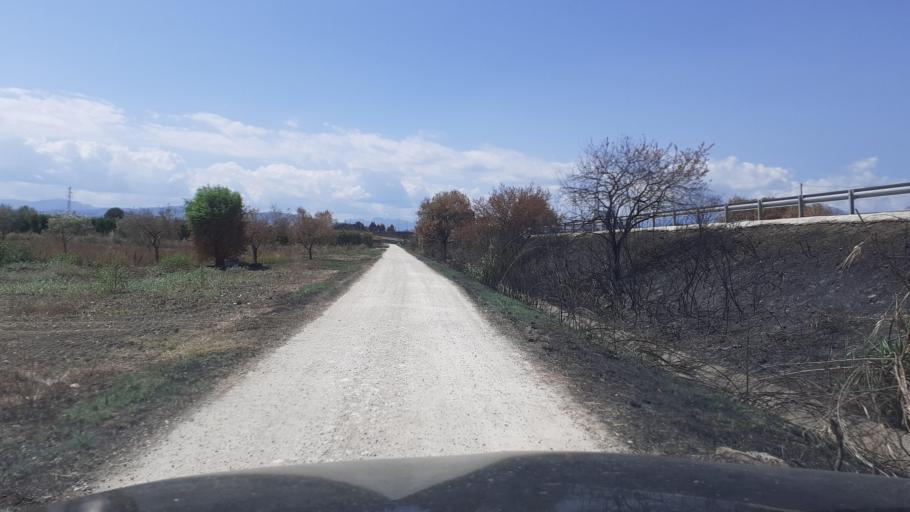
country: IT
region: Abruzzo
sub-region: Provincia di Chieti
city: Fossacesia
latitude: 42.2189
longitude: 14.4997
